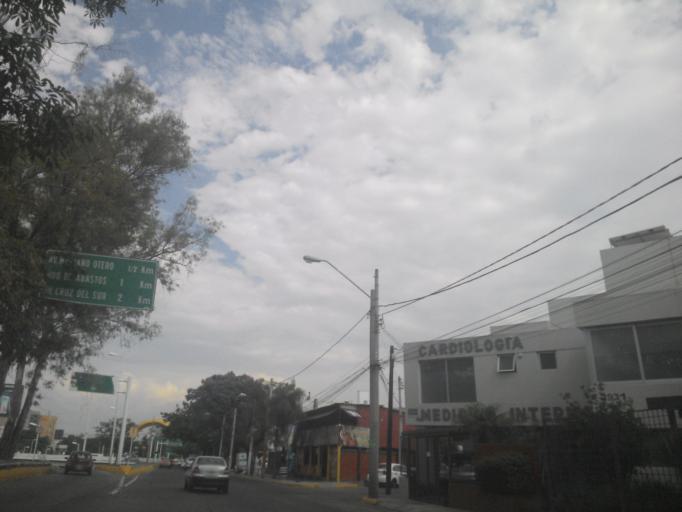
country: MX
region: Jalisco
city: Guadalajara
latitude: 20.6621
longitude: -103.3892
